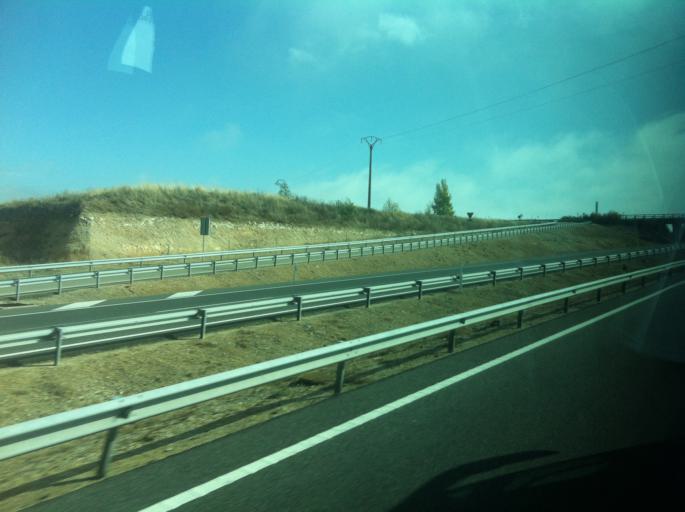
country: ES
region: Castille and Leon
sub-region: Provincia de Burgos
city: Oquillas
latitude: 41.8271
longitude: -3.7069
